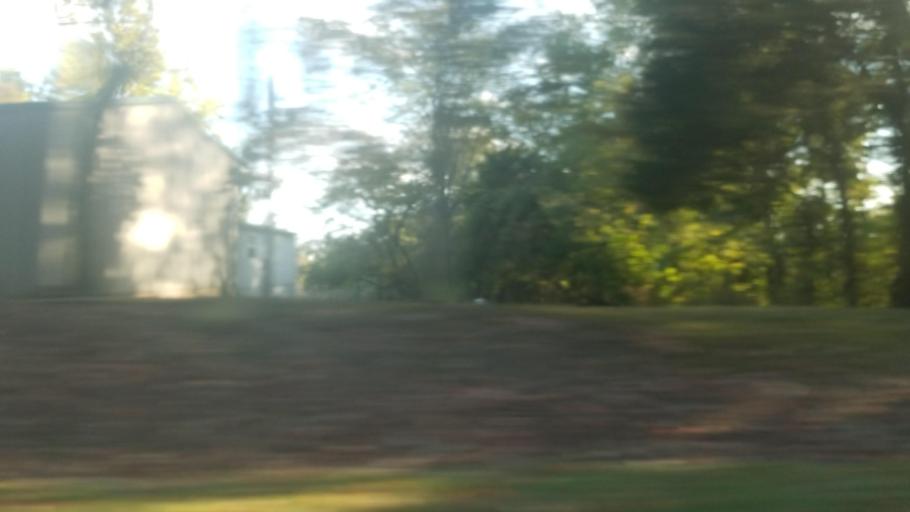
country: US
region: Illinois
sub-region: Saline County
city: Carrier Mills
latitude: 37.7717
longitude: -88.7504
